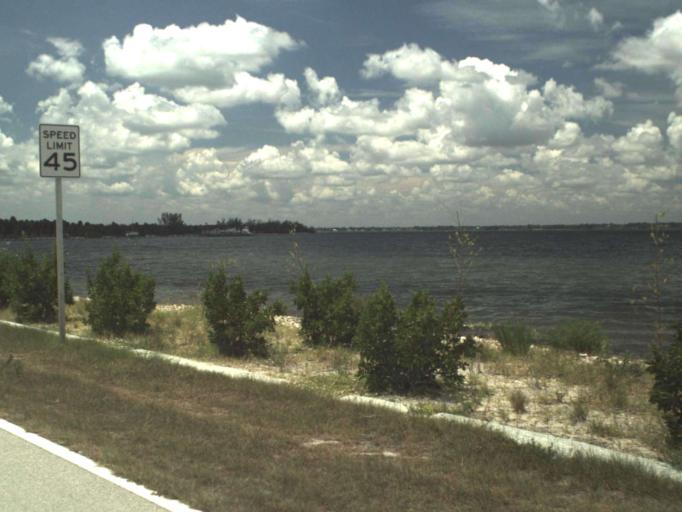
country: US
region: Florida
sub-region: Saint Lucie County
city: Hutchinson Island South
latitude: 27.3113
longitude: -80.2231
